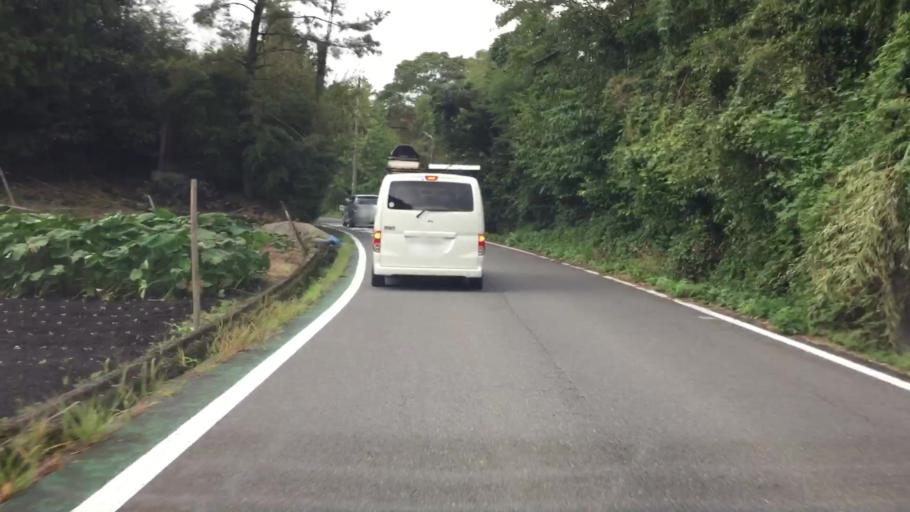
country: JP
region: Shizuoka
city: Fujinomiya
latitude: 35.3569
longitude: 138.5929
